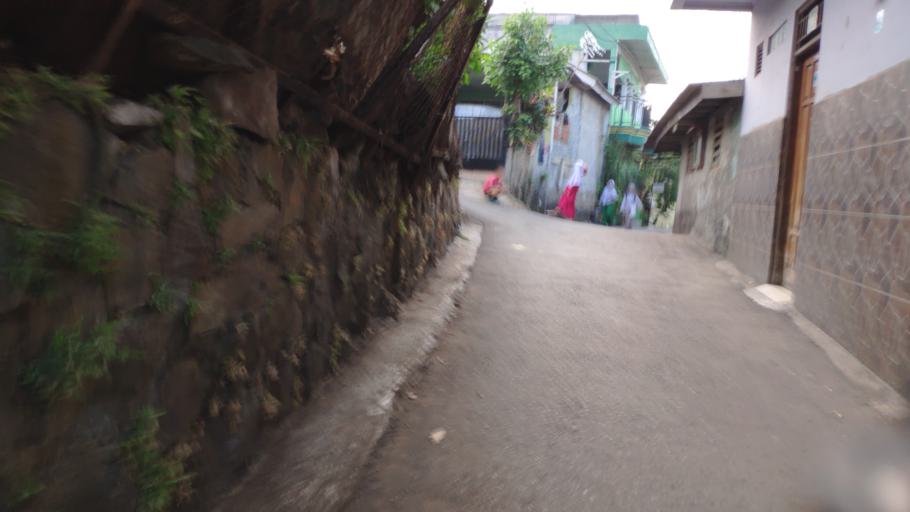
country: ID
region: Jakarta Raya
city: Jakarta
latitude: -6.2976
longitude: 106.8184
